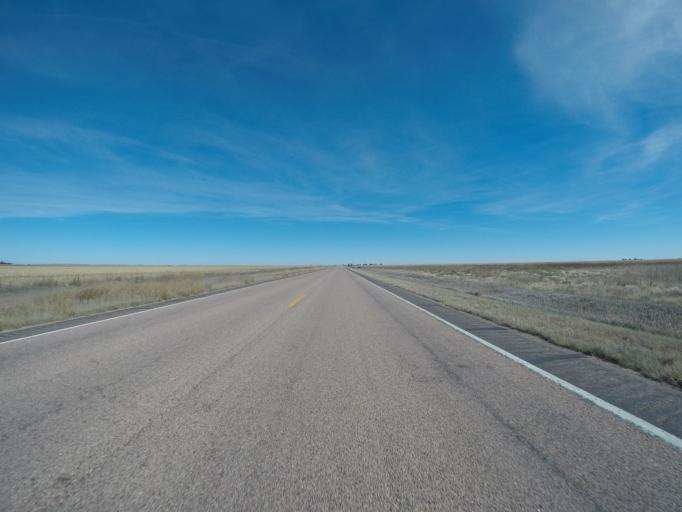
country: US
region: Colorado
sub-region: Yuma County
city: Yuma
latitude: 39.6562
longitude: -102.6017
